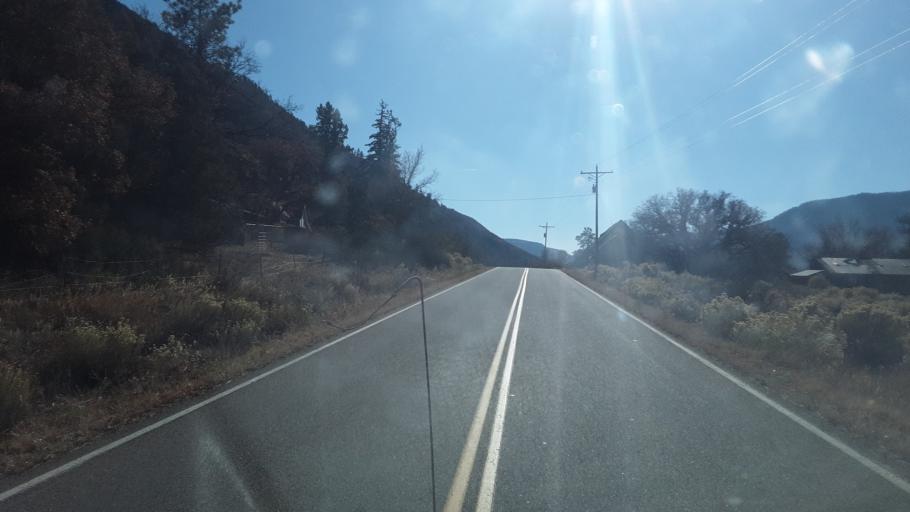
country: US
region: Colorado
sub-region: La Plata County
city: Durango
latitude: 37.3966
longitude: -107.8217
